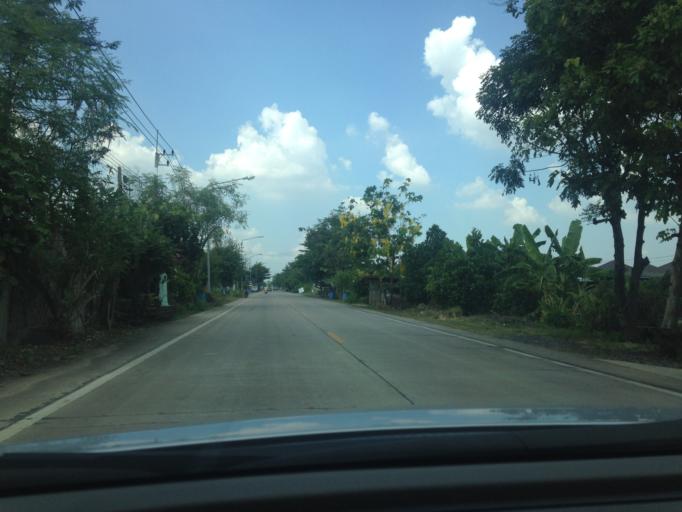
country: TH
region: Pathum Thani
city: Khlong Luang
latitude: 14.0433
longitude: 100.5916
